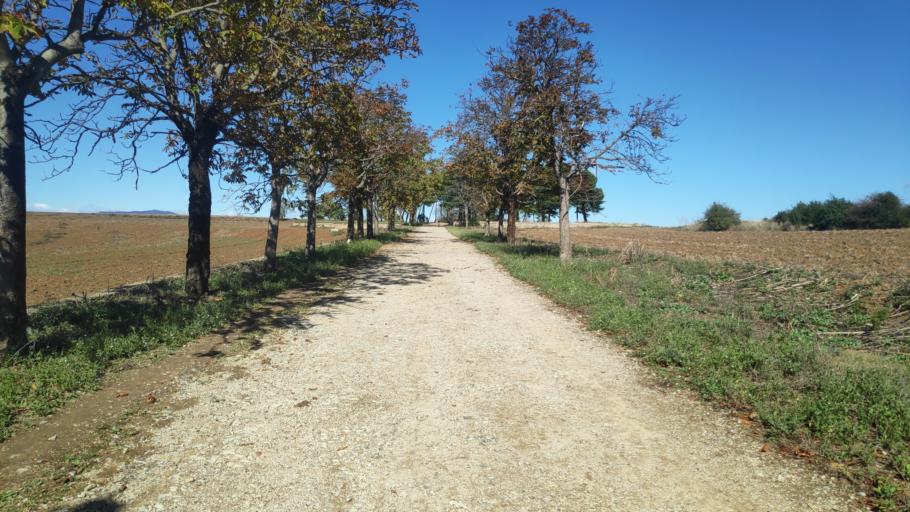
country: ES
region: Catalonia
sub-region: Provincia de Barcelona
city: Mollet del Valles
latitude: 41.5386
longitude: 2.2006
